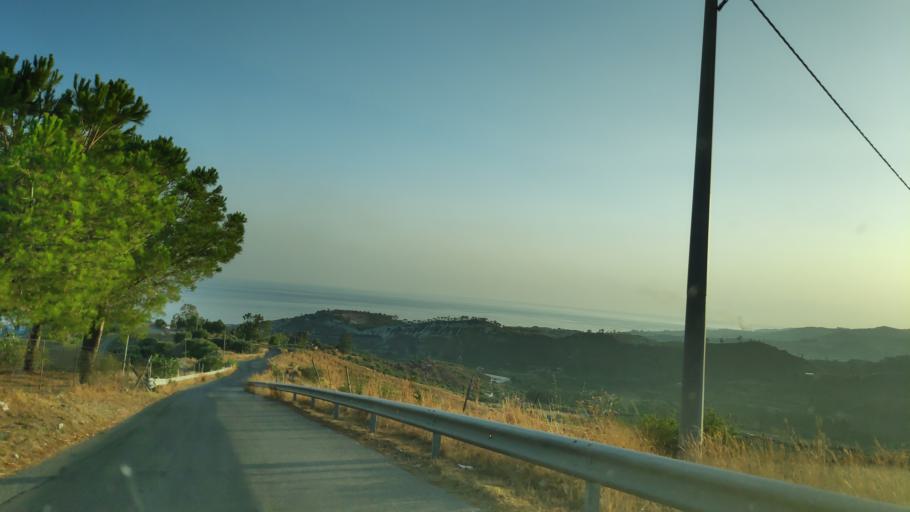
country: IT
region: Calabria
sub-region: Provincia di Reggio Calabria
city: Bova Marina
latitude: 37.9463
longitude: 15.9192
